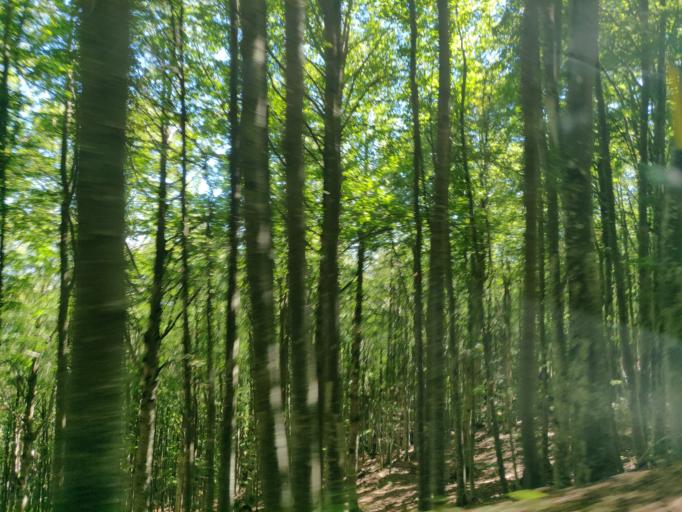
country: IT
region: Tuscany
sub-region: Provincia di Siena
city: Abbadia San Salvatore
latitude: 42.8865
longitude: 11.6273
